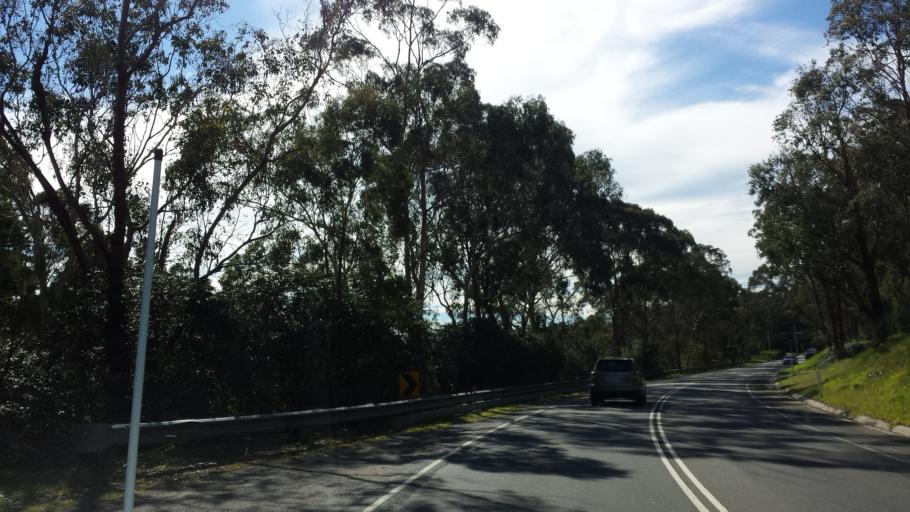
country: AU
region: Victoria
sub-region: Manningham
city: Park Orchards
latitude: -37.7717
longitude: 145.2295
